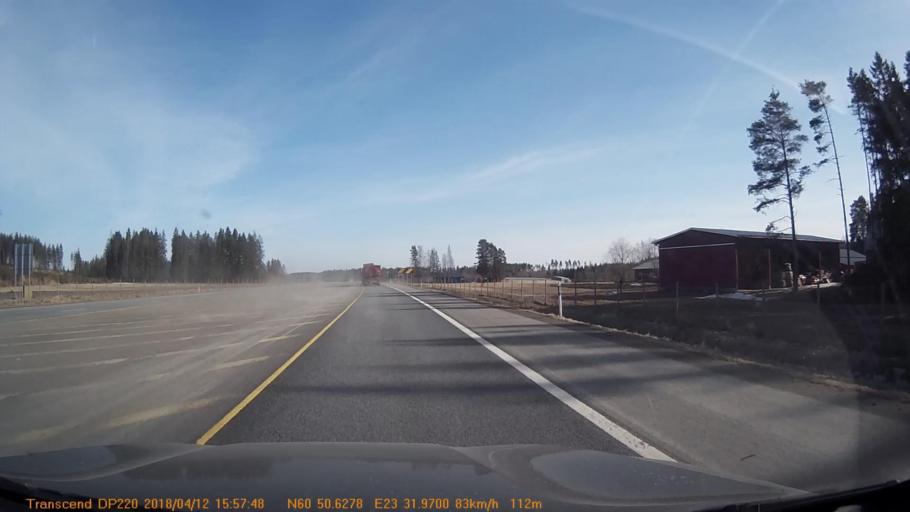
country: FI
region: Haeme
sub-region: Forssa
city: Jokioinen
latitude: 60.8433
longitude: 23.5336
